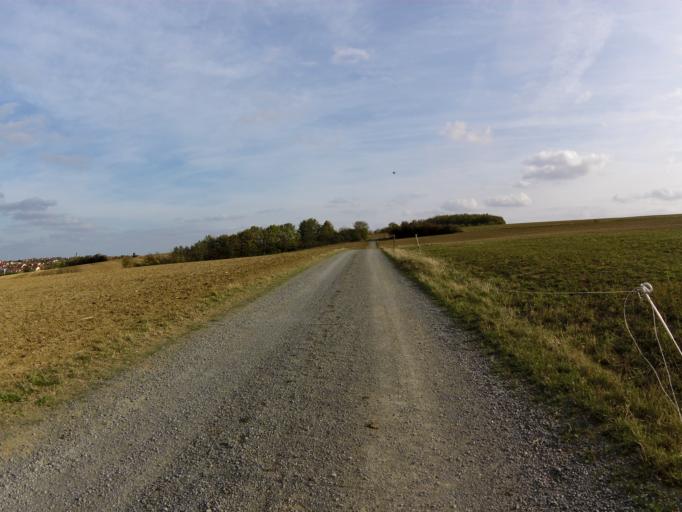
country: DE
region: Bavaria
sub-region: Regierungsbezirk Unterfranken
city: Reichenberg
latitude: 49.7236
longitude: 9.9474
